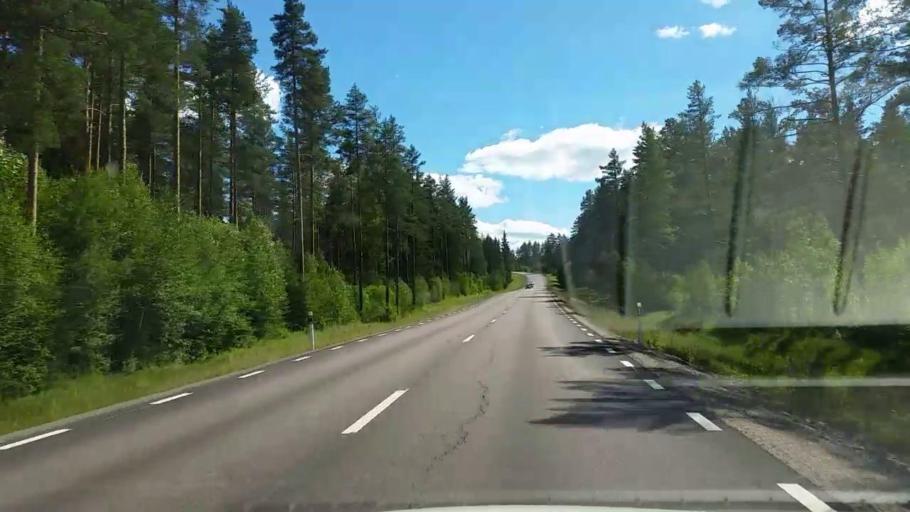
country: SE
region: Dalarna
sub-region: Faluns Kommun
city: Svardsjo
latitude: 60.7867
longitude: 15.7522
